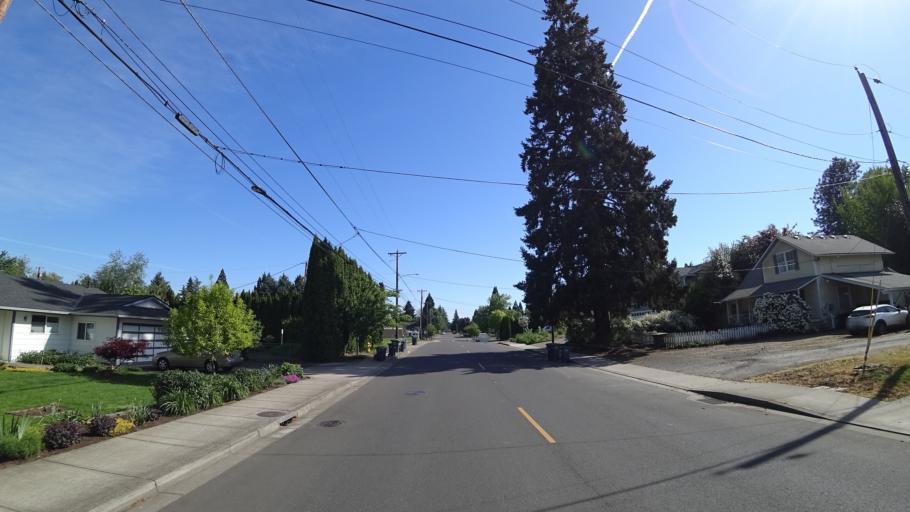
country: US
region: Oregon
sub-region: Washington County
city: Hillsboro
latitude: 45.5163
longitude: -122.9640
